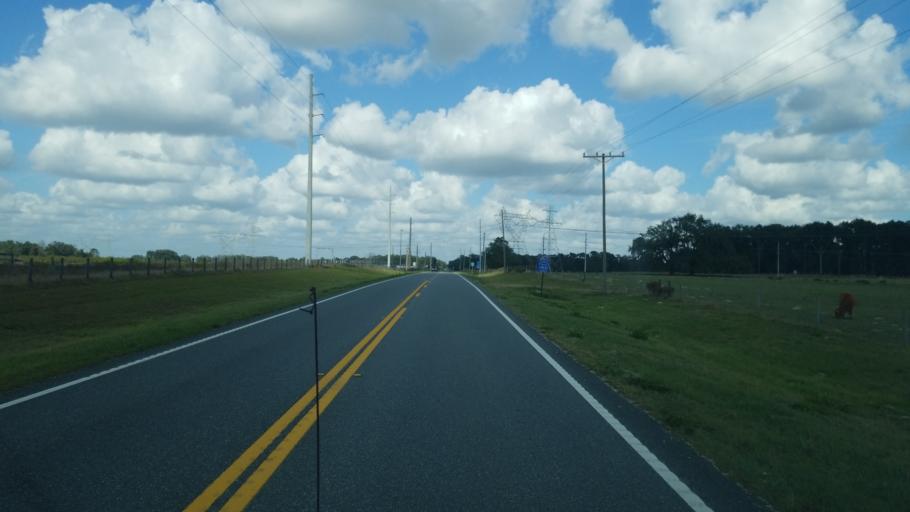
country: US
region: Florida
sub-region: Sumter County
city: Wildwood
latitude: 28.8922
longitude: -82.1200
